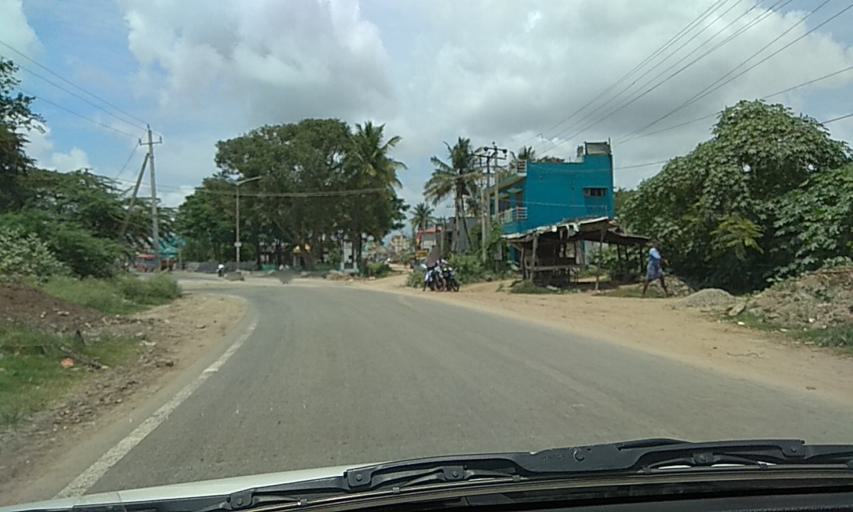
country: IN
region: Karnataka
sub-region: Chamrajnagar
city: Gundlupet
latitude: 11.8097
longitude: 76.6967
